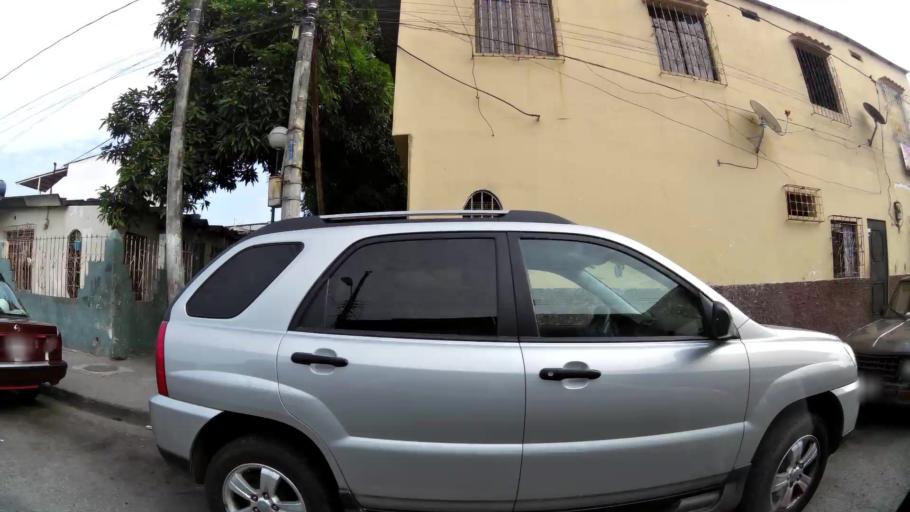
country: EC
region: Guayas
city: Guayaquil
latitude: -2.2539
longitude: -79.8850
